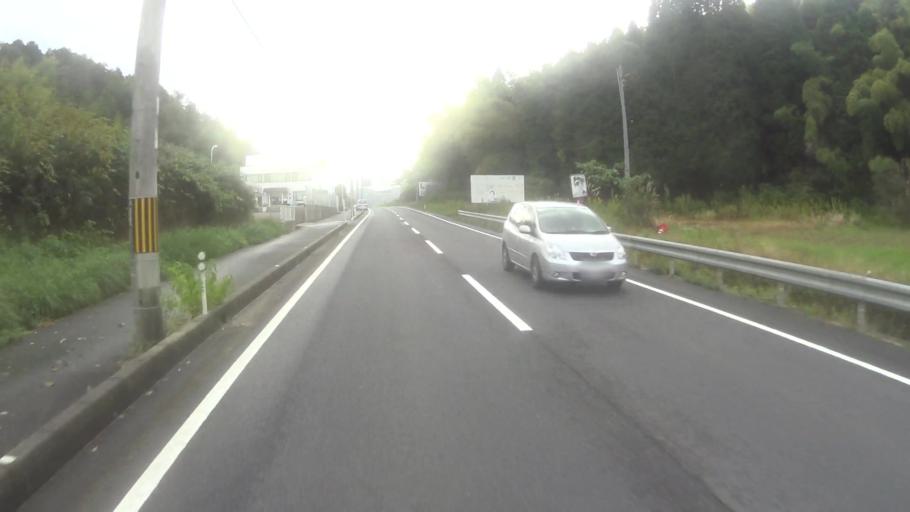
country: JP
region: Kyoto
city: Miyazu
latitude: 35.5242
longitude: 135.1145
